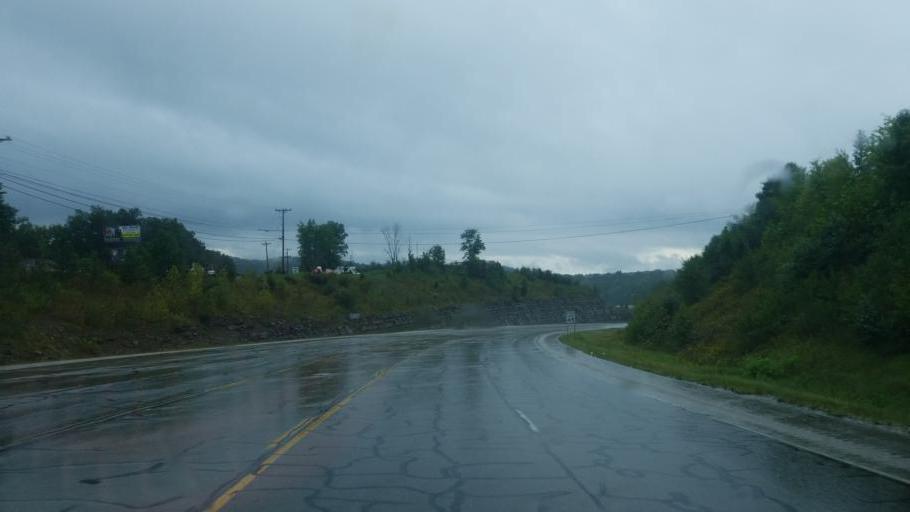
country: US
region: Kentucky
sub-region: Rowan County
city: Morehead
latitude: 38.2045
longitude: -83.4734
